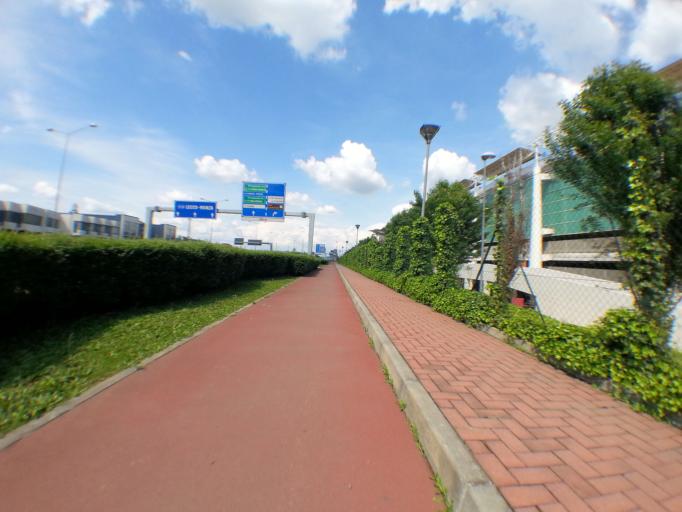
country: IT
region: Lombardy
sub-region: Citta metropolitana di Milano
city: Cinisello Balsamo
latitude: 45.5565
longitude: 9.2405
